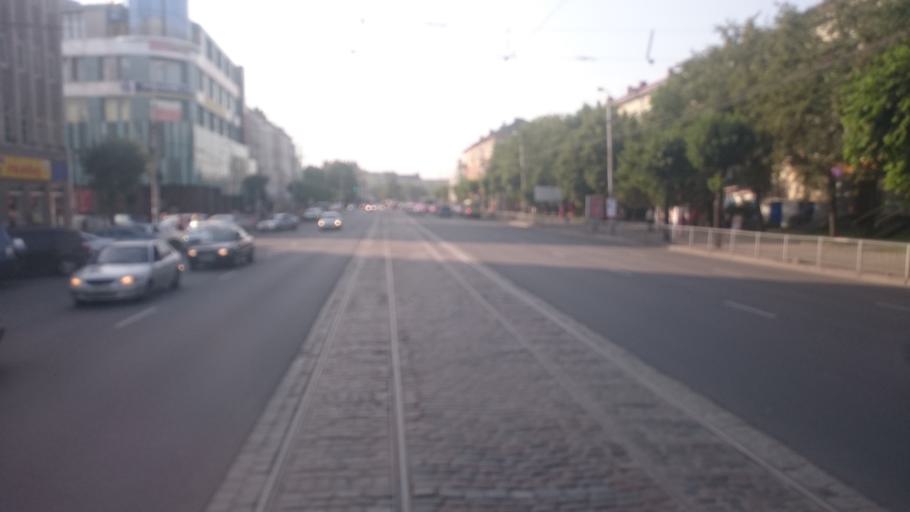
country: RU
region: Kaliningrad
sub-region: Gorod Kaliningrad
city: Kaliningrad
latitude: 54.7138
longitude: 20.5061
